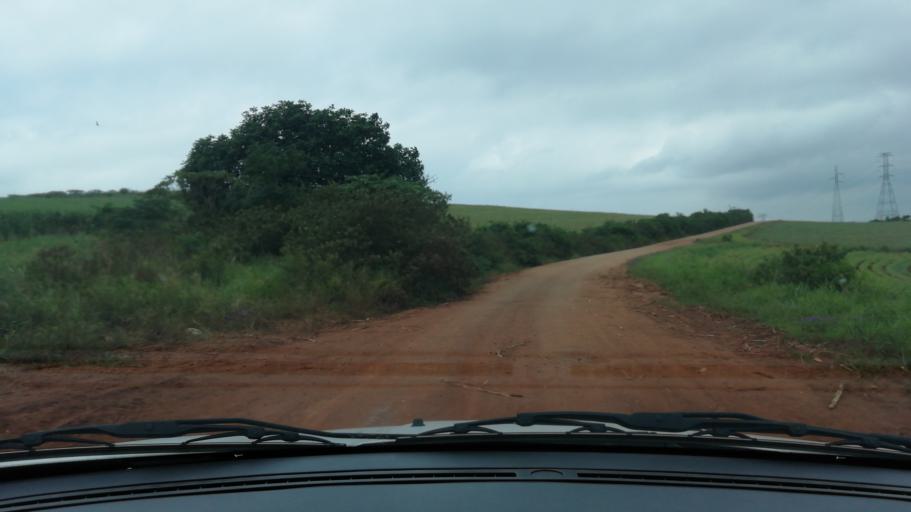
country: ZA
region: KwaZulu-Natal
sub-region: uThungulu District Municipality
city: Empangeni
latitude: -28.7297
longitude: 31.9045
